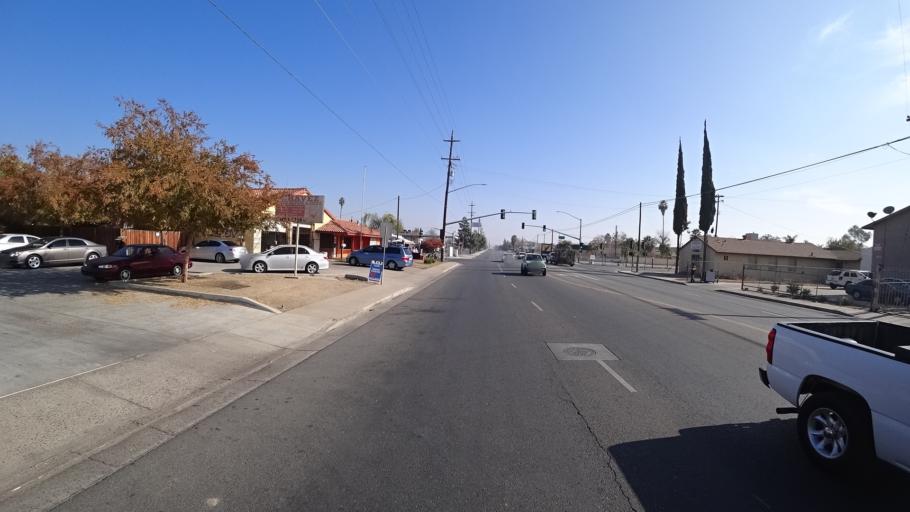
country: US
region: California
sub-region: Kern County
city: Bakersfield
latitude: 35.3540
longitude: -118.9949
